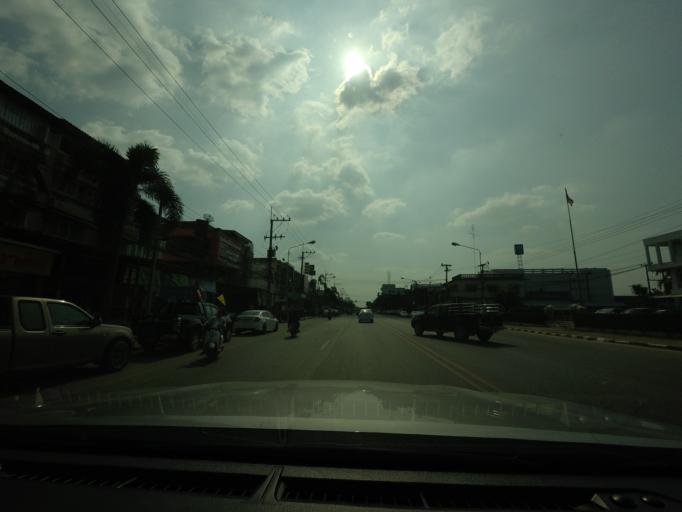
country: TH
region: Phitsanulok
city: Bang Rakam
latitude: 16.7575
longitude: 100.1181
